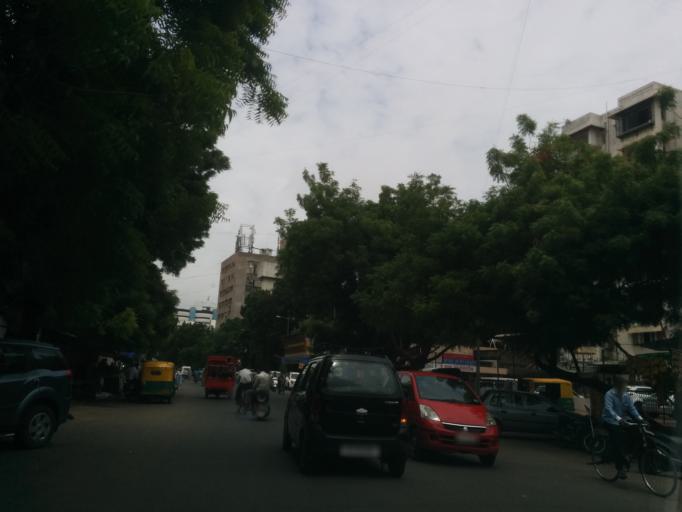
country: IN
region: Gujarat
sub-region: Ahmadabad
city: Ahmedabad
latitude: 23.0323
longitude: 72.5620
